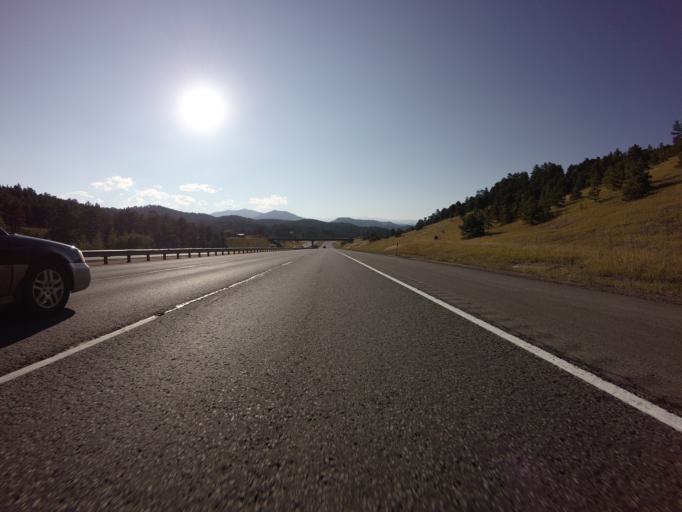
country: US
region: Colorado
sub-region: Jefferson County
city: Kittredge
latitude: 39.7021
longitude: -105.3357
